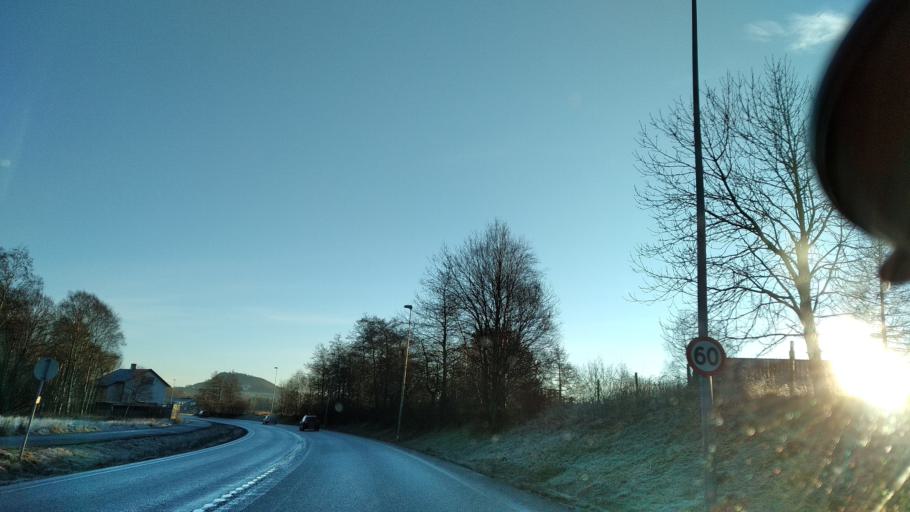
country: NO
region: Rogaland
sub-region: Stavanger
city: Stavanger
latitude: 58.9255
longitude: 5.6987
